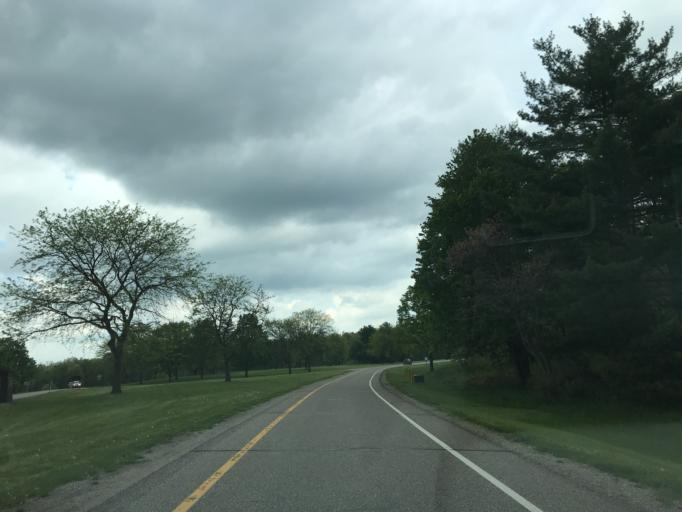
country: US
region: Michigan
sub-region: Oakland County
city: Milford
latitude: 42.5460
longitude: -83.6288
